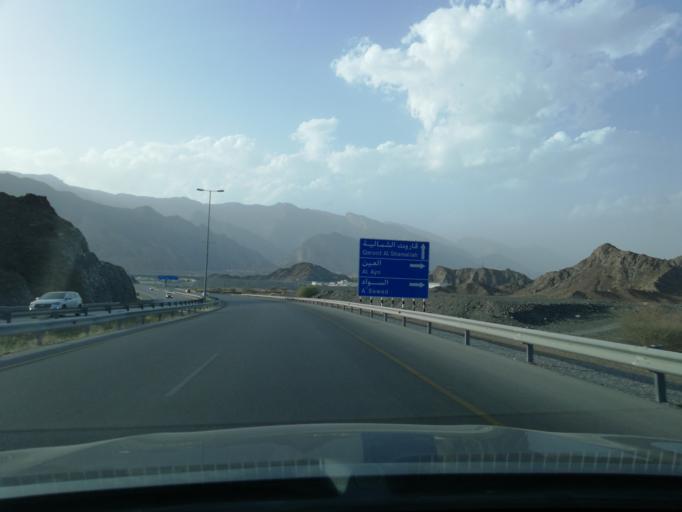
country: OM
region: Muhafazat ad Dakhiliyah
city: Izki
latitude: 22.9675
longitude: 57.7834
